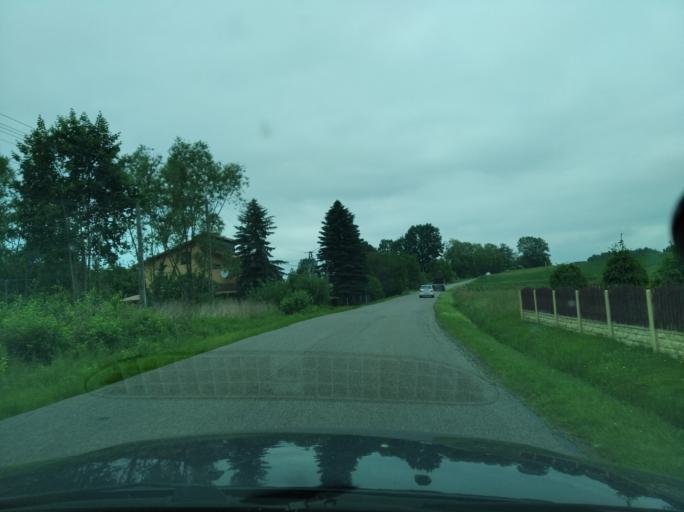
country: PL
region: Subcarpathian Voivodeship
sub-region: Powiat kolbuszowski
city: Niwiska
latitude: 50.1587
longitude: 21.6672
